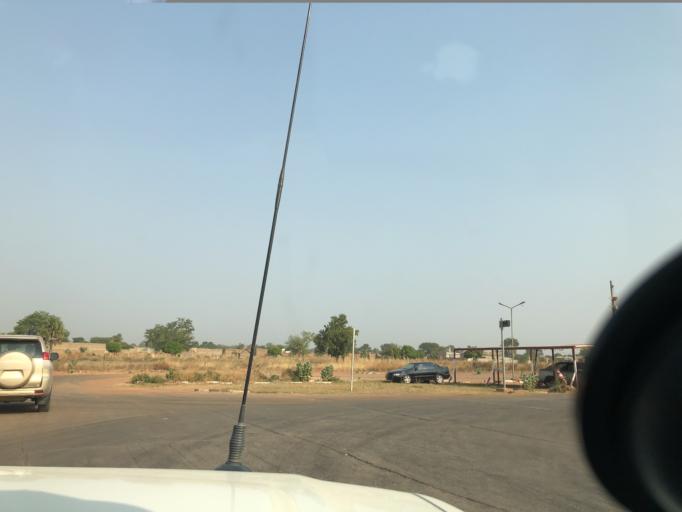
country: TD
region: Logone Occidental
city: Moundou
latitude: 8.5886
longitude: 16.0242
